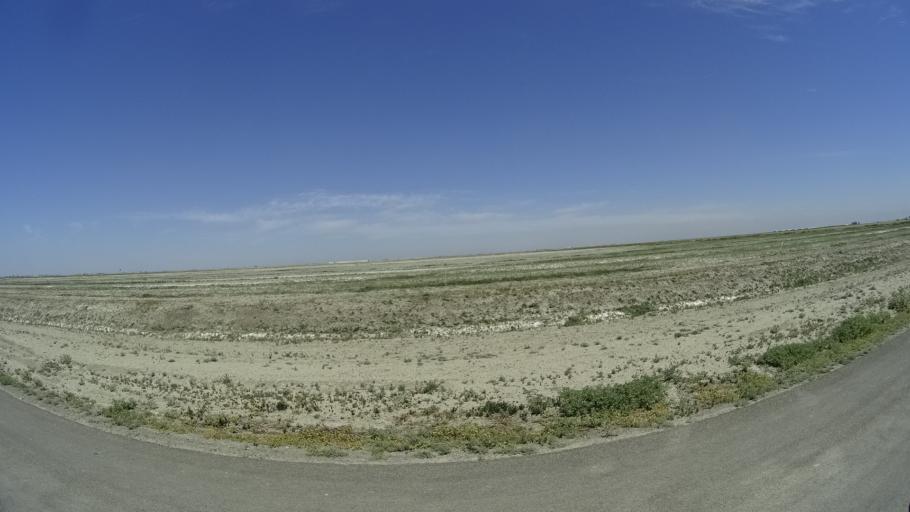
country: US
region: California
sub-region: Kings County
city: Corcoran
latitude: 36.1233
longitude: -119.6836
